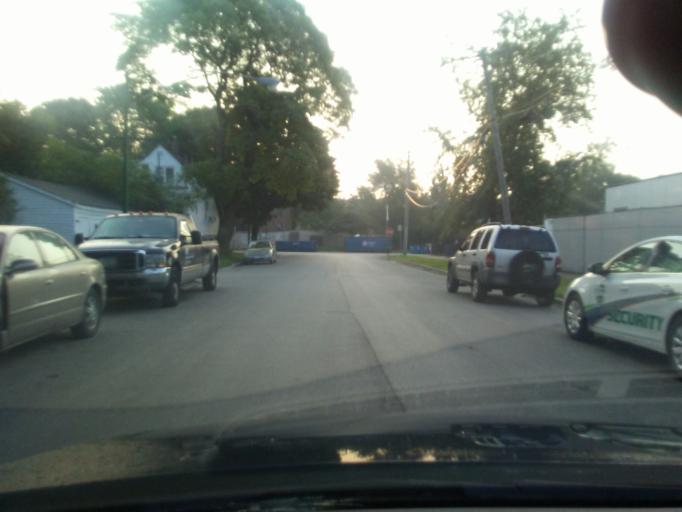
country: US
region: Illinois
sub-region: Cook County
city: Lincolnwood
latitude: 41.9349
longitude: -87.6839
